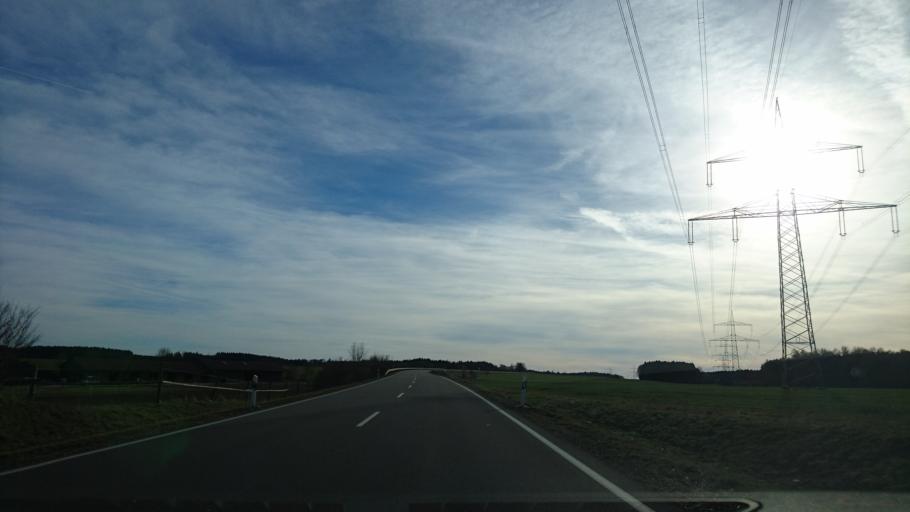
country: DE
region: Bavaria
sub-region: Swabia
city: Biberbach
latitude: 48.5311
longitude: 10.7572
